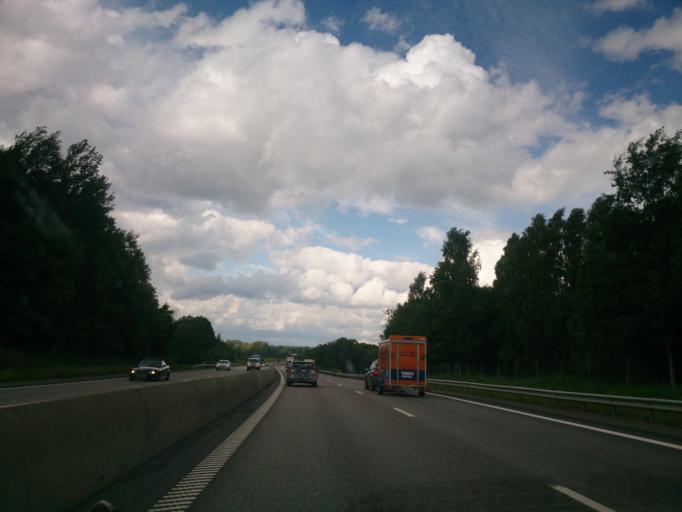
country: SE
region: OEstergoetland
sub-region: Norrkopings Kommun
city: Norrkoping
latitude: 58.5936
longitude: 16.1286
